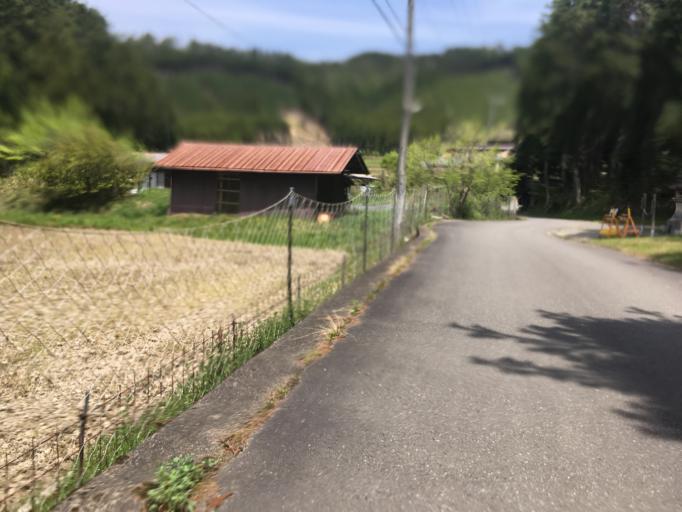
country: JP
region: Kyoto
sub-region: Kyoto-shi
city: Kamigyo-ku
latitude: 35.0834
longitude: 135.7220
